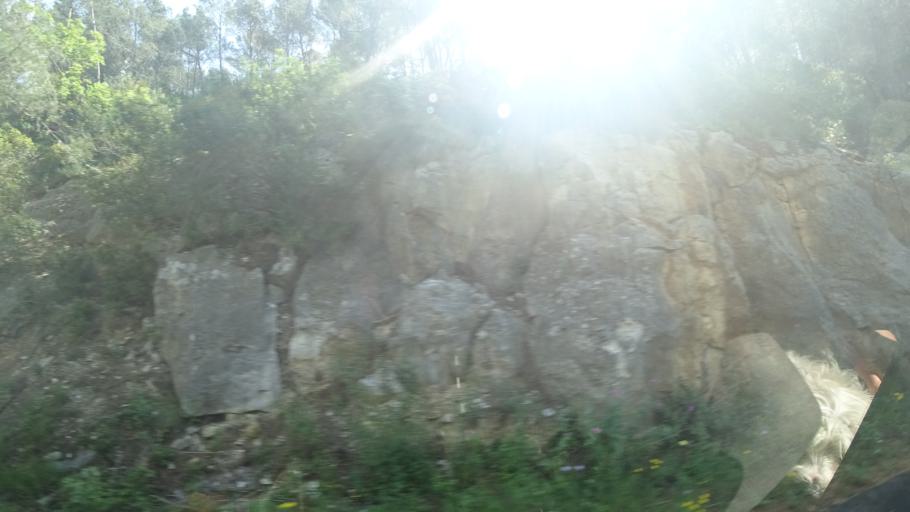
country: FR
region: Languedoc-Roussillon
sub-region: Departement de l'Herault
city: Olonzac
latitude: 43.3508
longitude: 2.7568
